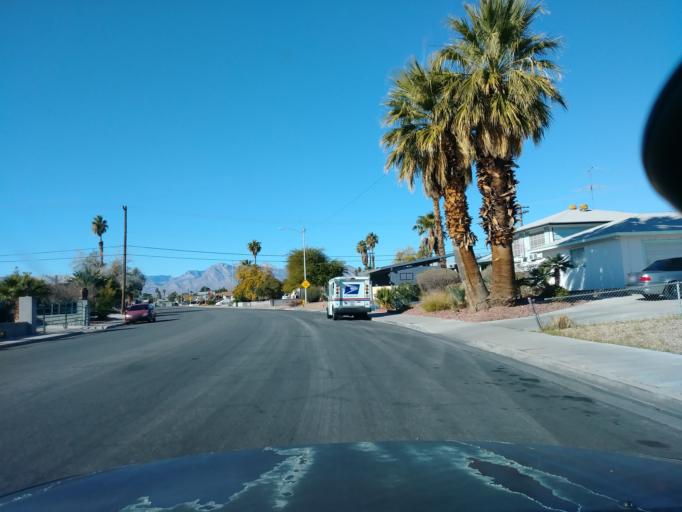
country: US
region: Nevada
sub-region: Clark County
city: Spring Valley
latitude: 36.1757
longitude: -115.2292
